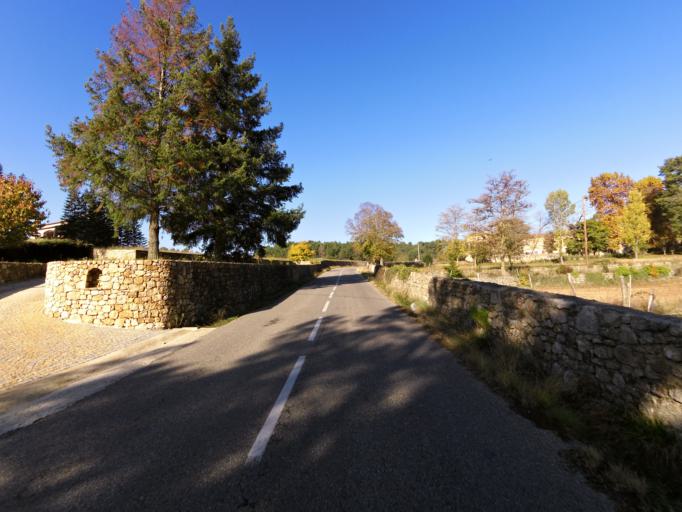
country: FR
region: Rhone-Alpes
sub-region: Departement de l'Ardeche
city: Lablachere
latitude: 44.4688
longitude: 4.2049
